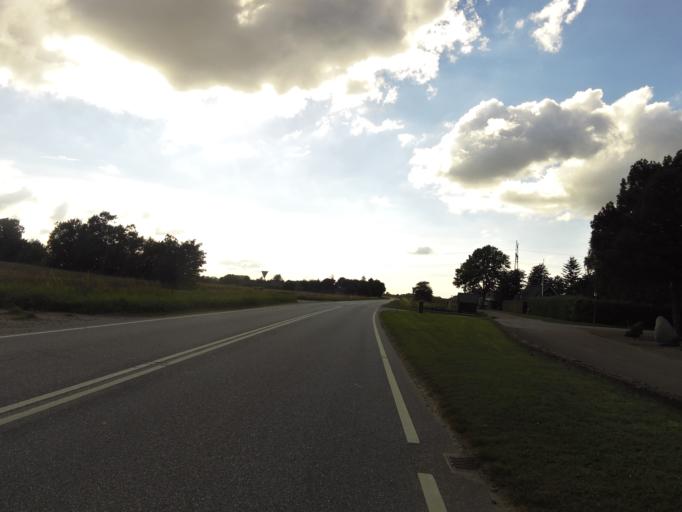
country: DK
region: South Denmark
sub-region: Haderslev Kommune
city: Vojens
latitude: 55.1969
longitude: 9.3291
